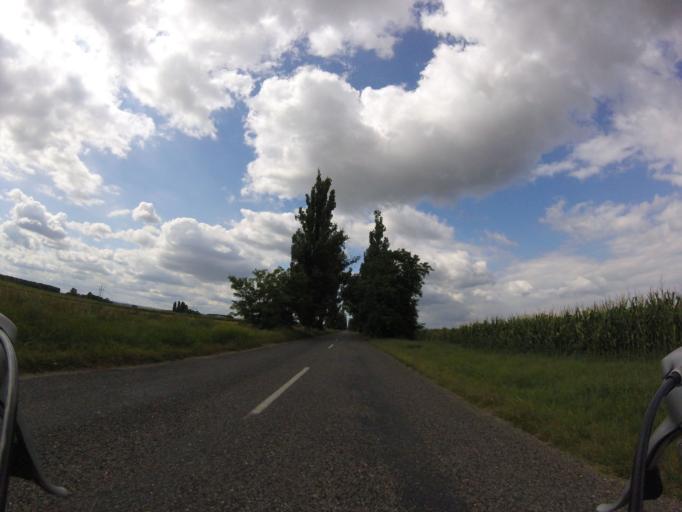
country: HU
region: Fejer
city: Seregelyes
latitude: 47.1622
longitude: 18.5766
